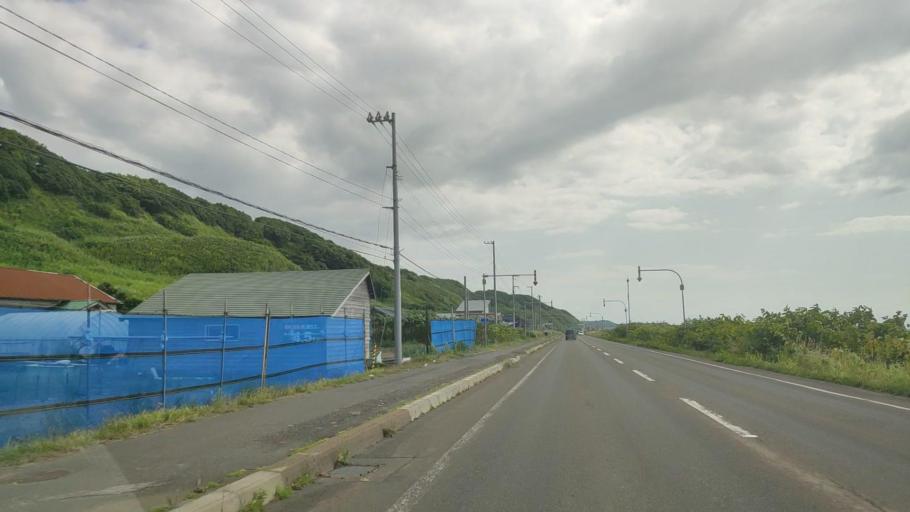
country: JP
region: Hokkaido
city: Rumoi
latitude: 44.1863
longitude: 141.6587
